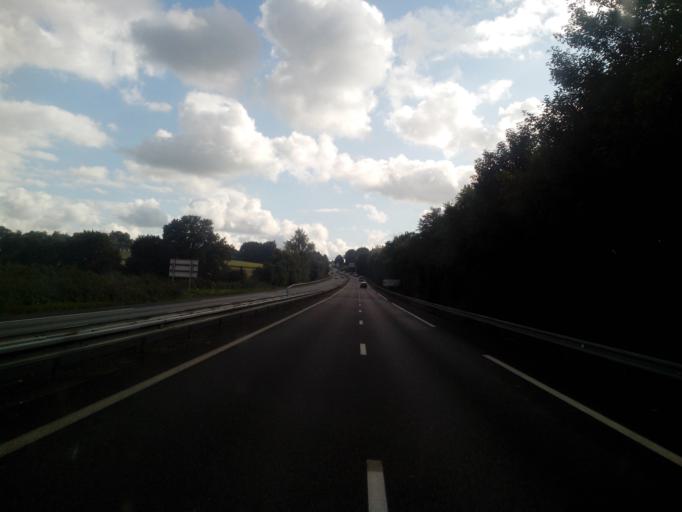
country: FR
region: Brittany
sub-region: Departement du Morbihan
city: Ploermel
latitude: 47.8775
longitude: -2.4175
